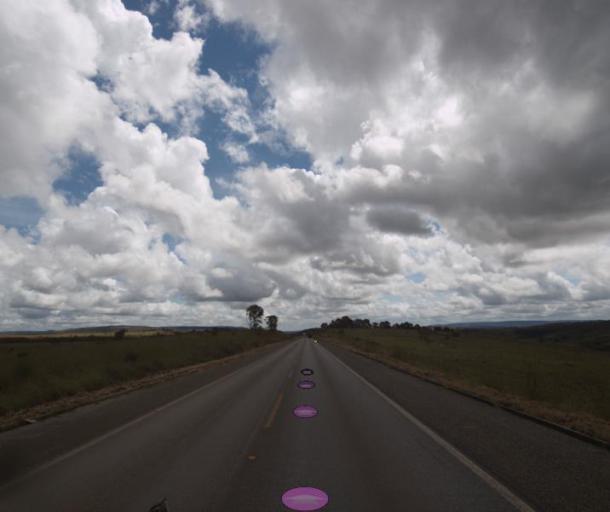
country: BR
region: Goias
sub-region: Pirenopolis
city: Pirenopolis
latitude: -15.7570
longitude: -48.7412
